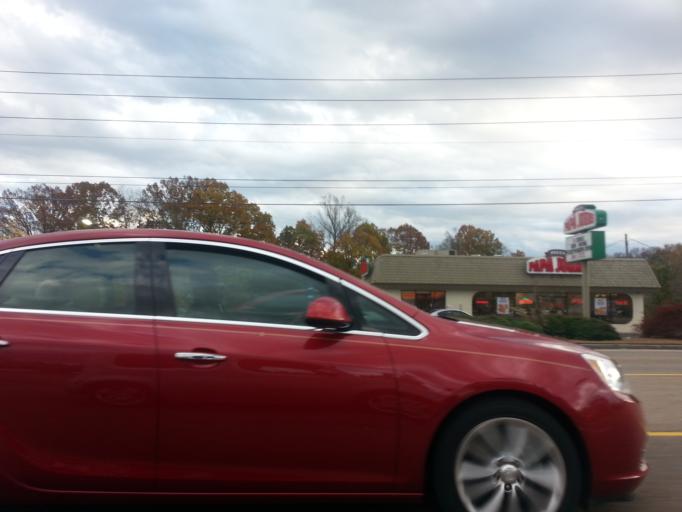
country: US
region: Tennessee
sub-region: Knox County
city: Knoxville
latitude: 35.9316
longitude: -84.0243
